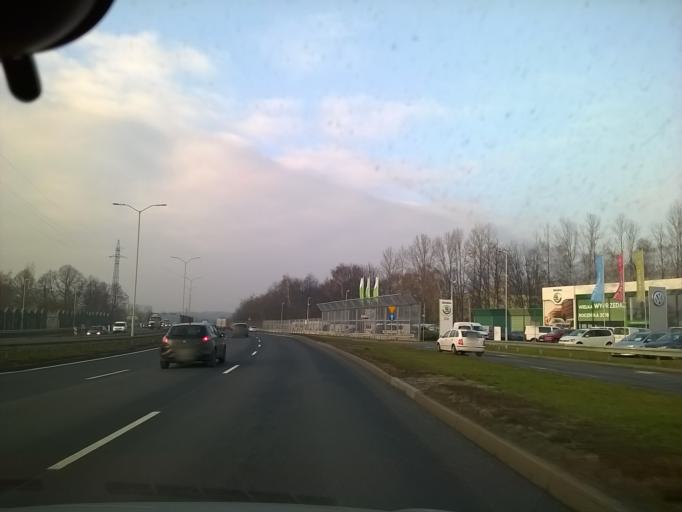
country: PL
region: Silesian Voivodeship
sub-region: Swietochlowice
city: Swietochlowice
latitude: 50.2910
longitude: 18.9314
